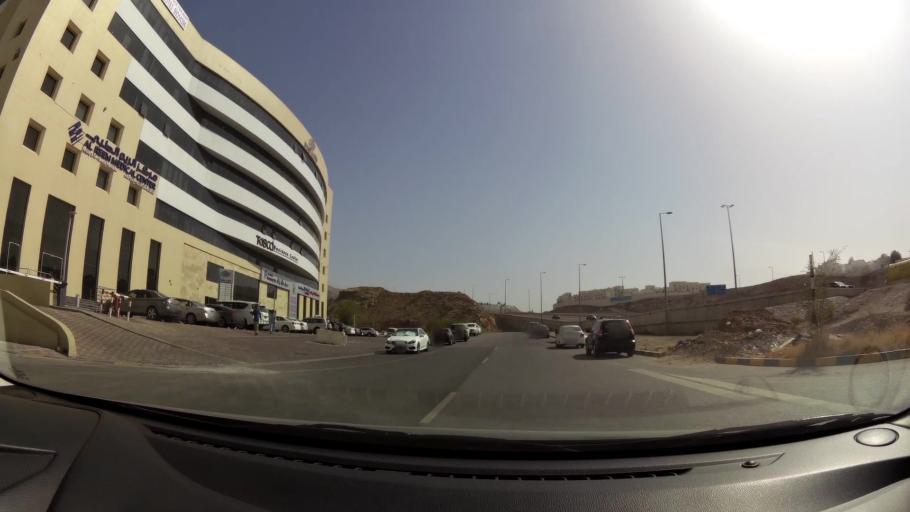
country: OM
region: Muhafazat Masqat
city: Muscat
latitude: 23.6051
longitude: 58.4909
